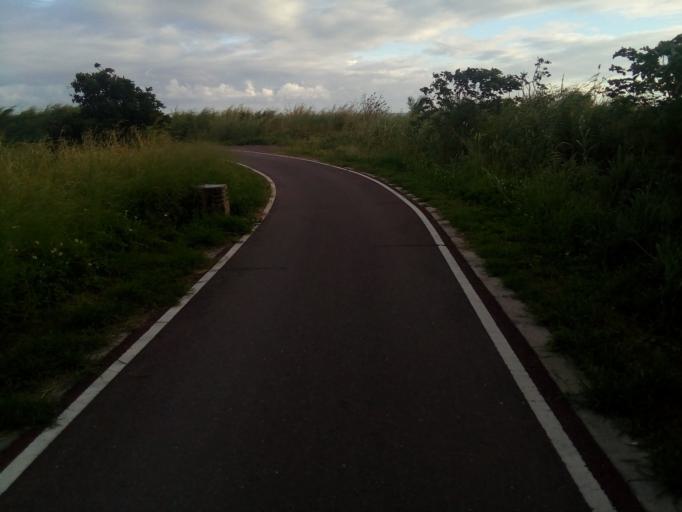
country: TW
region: Taiwan
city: Taitung City
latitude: 22.7507
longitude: 121.1595
